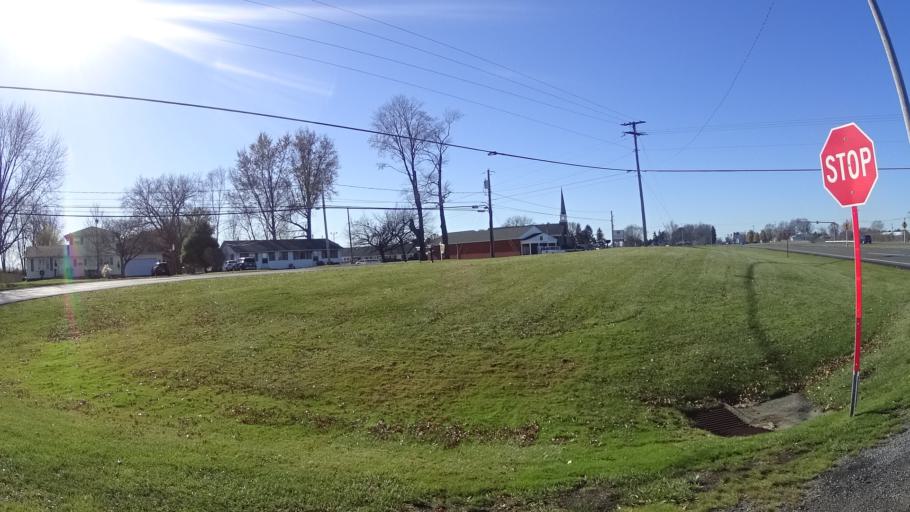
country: US
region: Ohio
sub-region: Lorain County
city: Elyria
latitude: 41.3757
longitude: -82.1582
